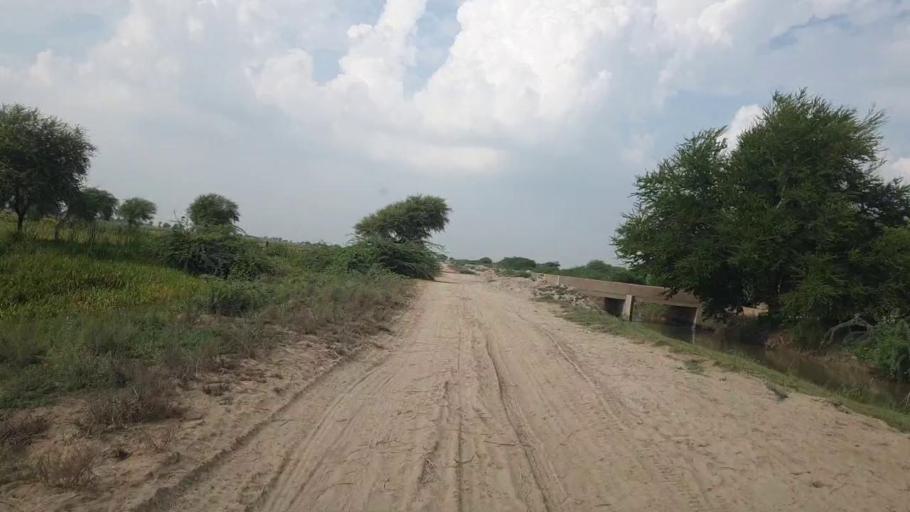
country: PK
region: Sindh
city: Badin
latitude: 24.5671
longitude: 68.6352
